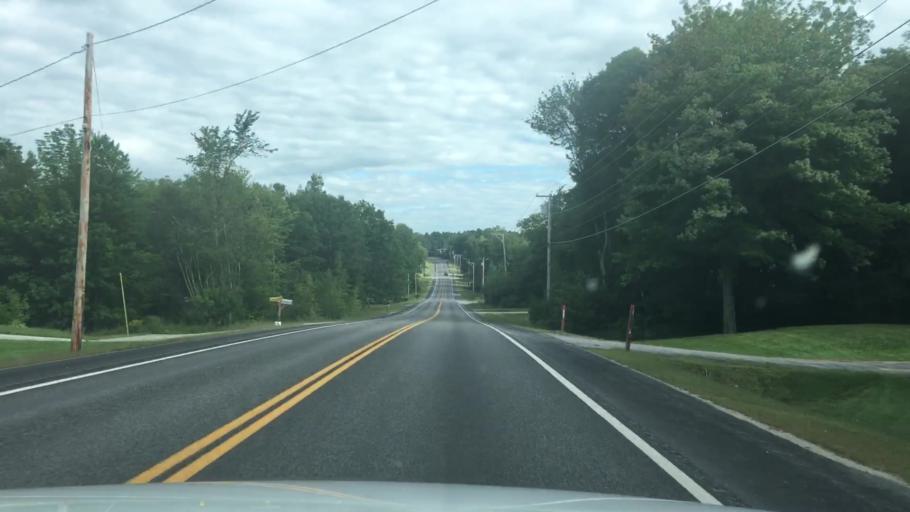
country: US
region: Maine
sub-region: Androscoggin County
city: Sabattus
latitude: 44.0780
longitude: -70.0794
